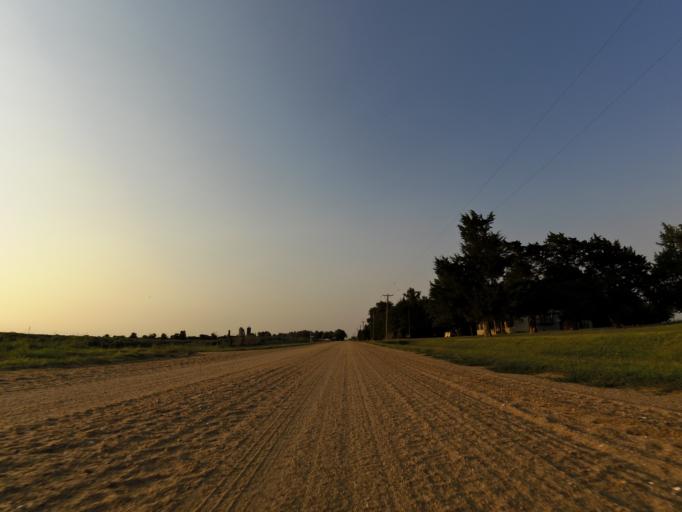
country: US
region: Kansas
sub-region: Reno County
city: South Hutchinson
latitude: 38.0084
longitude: -97.9954
